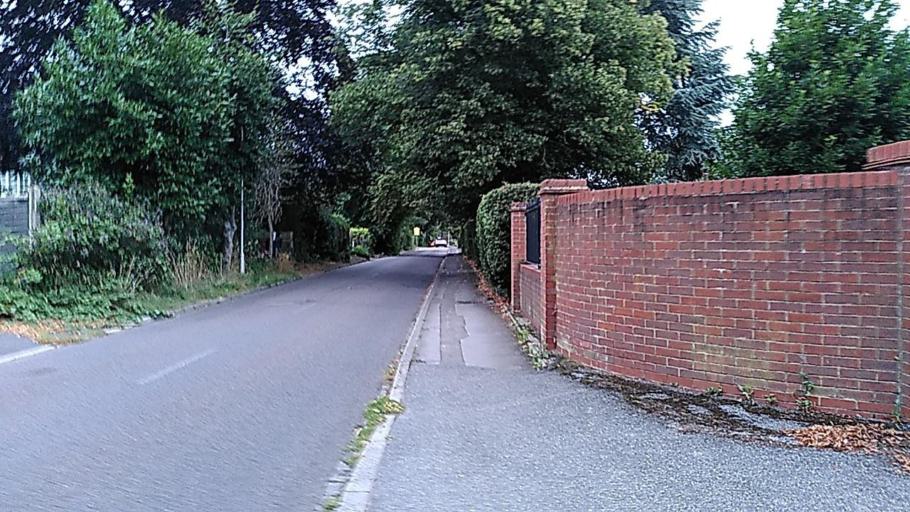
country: GB
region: England
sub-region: Reading
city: Reading
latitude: 51.4835
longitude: -0.9732
